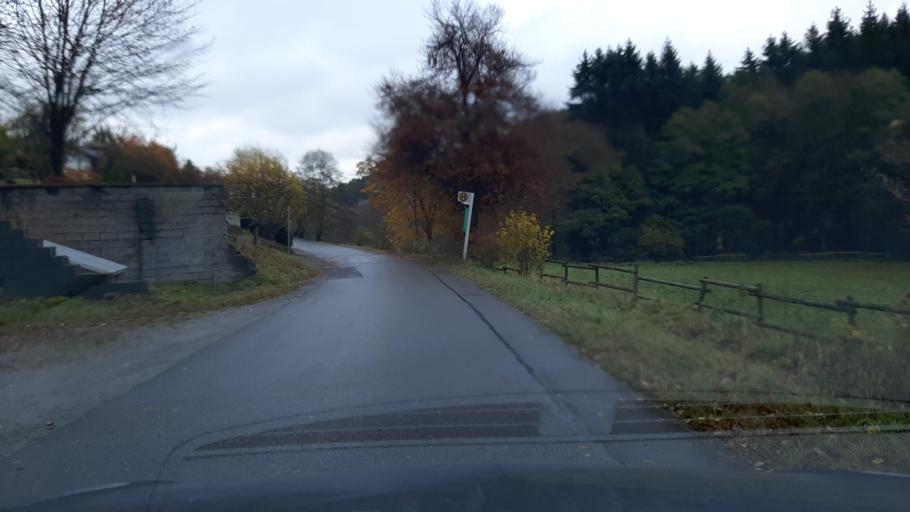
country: DE
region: Hesse
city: Willingen
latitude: 51.2867
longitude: 8.5818
